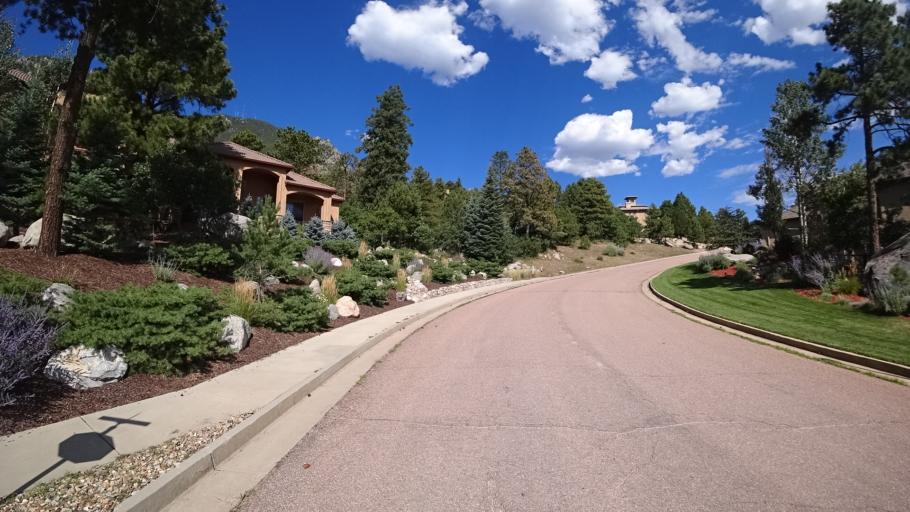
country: US
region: Colorado
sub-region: El Paso County
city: Fort Carson
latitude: 38.7466
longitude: -104.8382
